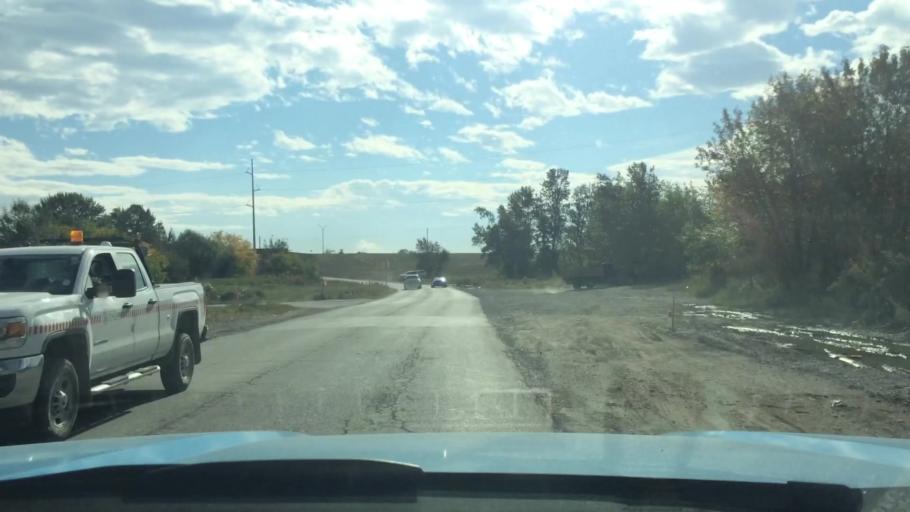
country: CA
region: Alberta
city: Calgary
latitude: 51.0085
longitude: -114.0299
